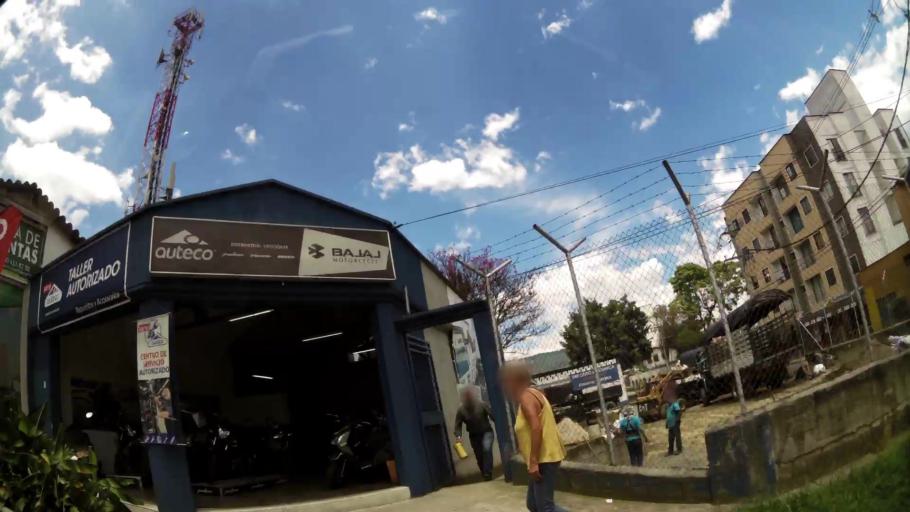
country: CO
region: Antioquia
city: La Estrella
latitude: 6.1597
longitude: -75.6429
